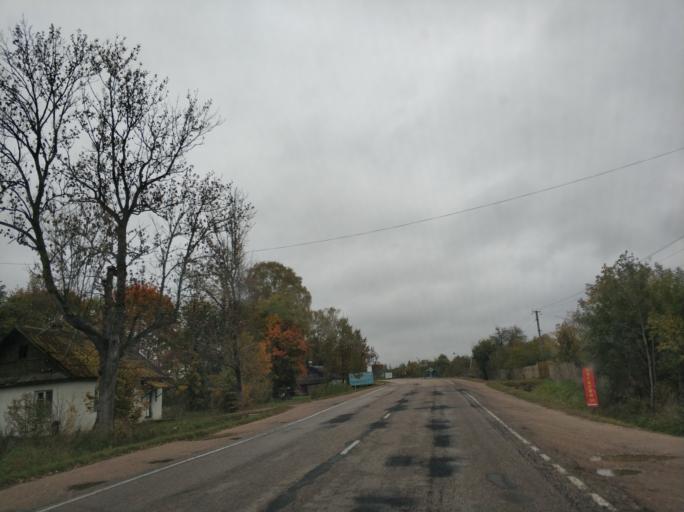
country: BY
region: Vitebsk
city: Rasony
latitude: 56.0550
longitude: 28.7122
